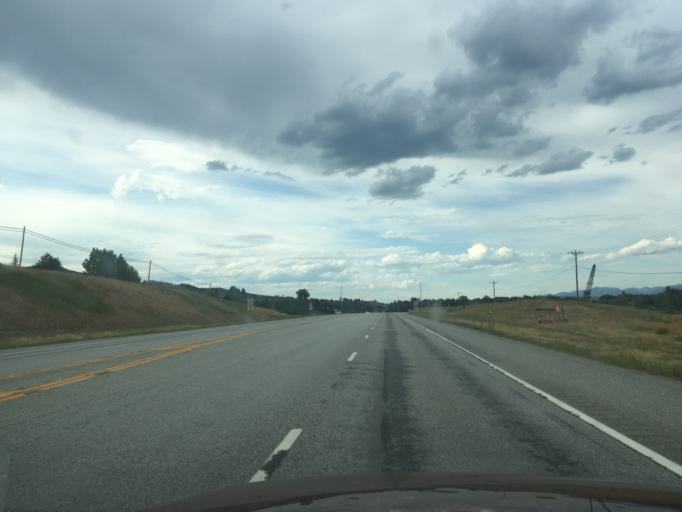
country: US
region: Montana
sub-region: Missoula County
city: Lolo
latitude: 46.7393
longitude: -114.0809
